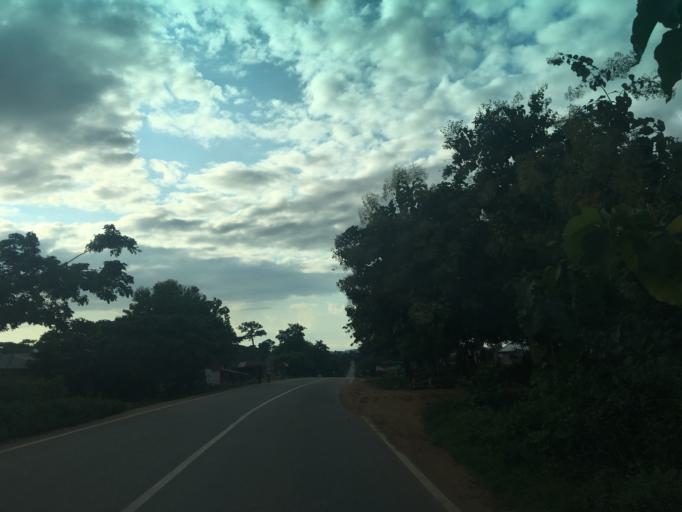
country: GH
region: Western
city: Bibiani
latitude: 6.3543
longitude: -2.2810
